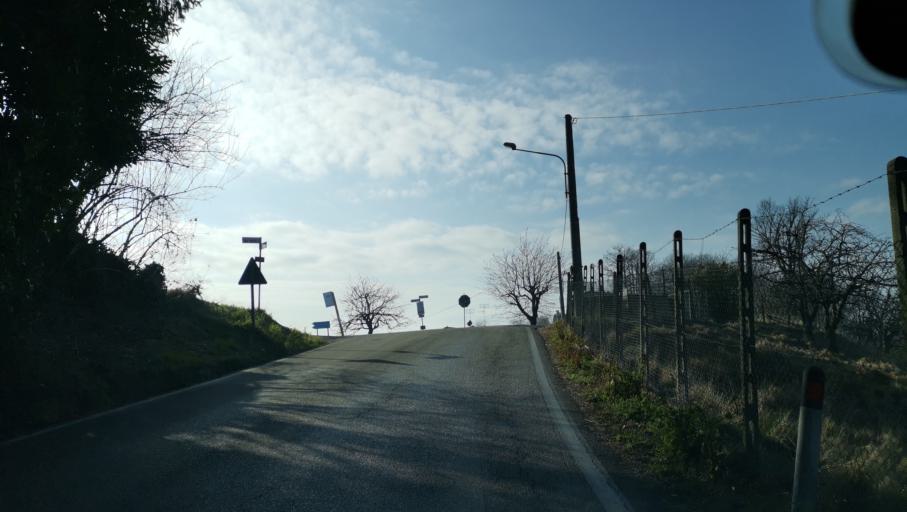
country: IT
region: Piedmont
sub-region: Provincia di Torino
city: Castagneto Po
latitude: 45.1440
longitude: 7.8756
